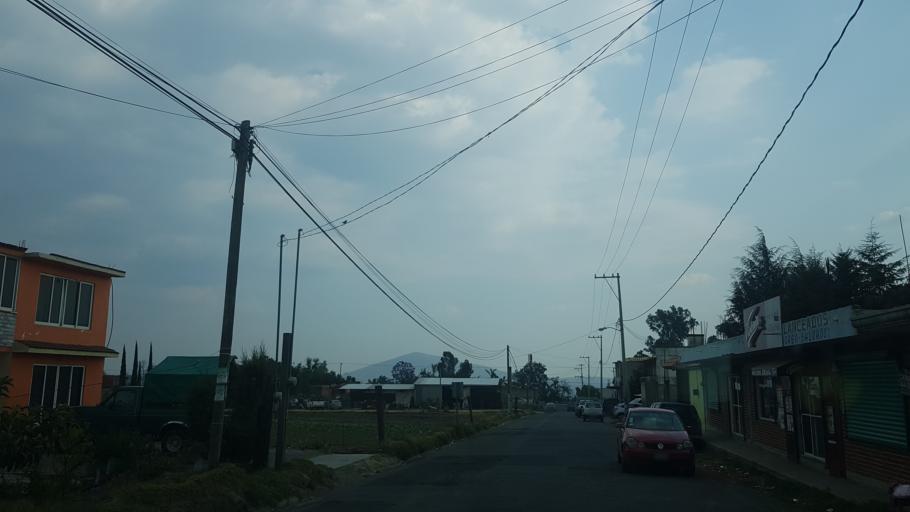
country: MX
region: Puebla
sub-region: Santa Isabel Cholula
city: Santa Ana Acozautla
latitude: 18.9456
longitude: -98.3947
